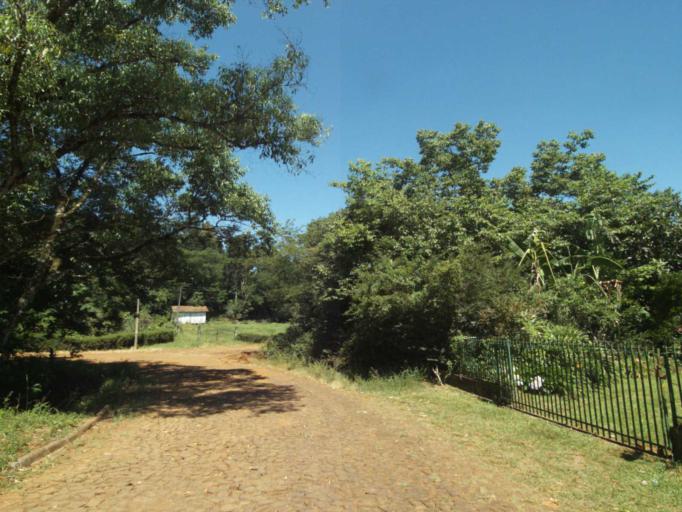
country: BR
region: Parana
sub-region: Laranjeiras Do Sul
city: Laranjeiras do Sul
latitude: -25.3812
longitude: -52.1962
